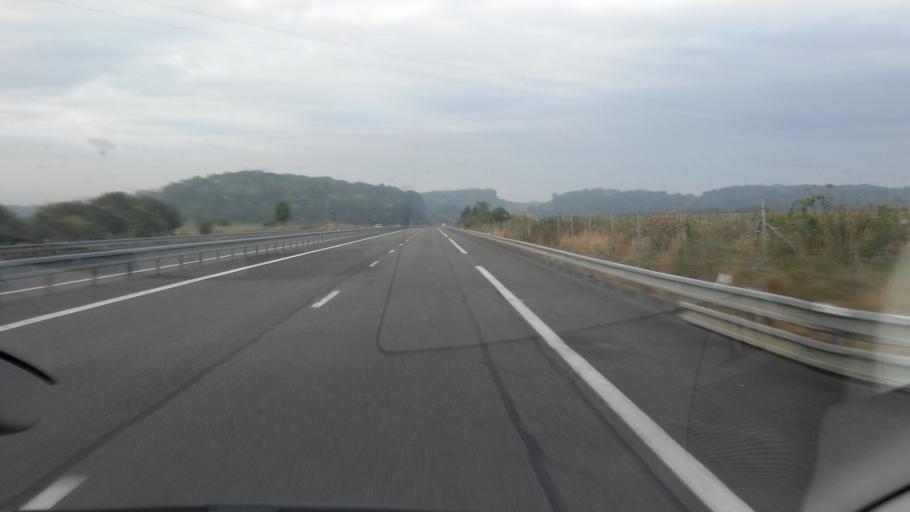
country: FR
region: Champagne-Ardenne
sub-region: Departement des Ardennes
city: Attigny
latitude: 49.6244
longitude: 4.5514
